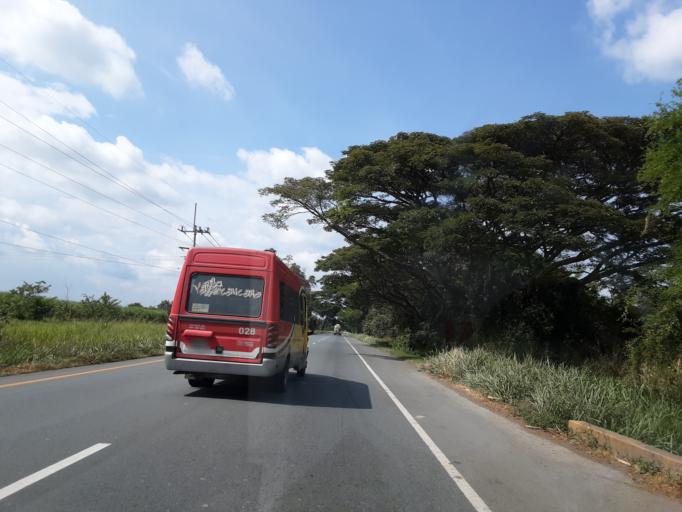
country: CO
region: Valle del Cauca
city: Guacari
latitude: 3.7488
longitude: -76.3252
